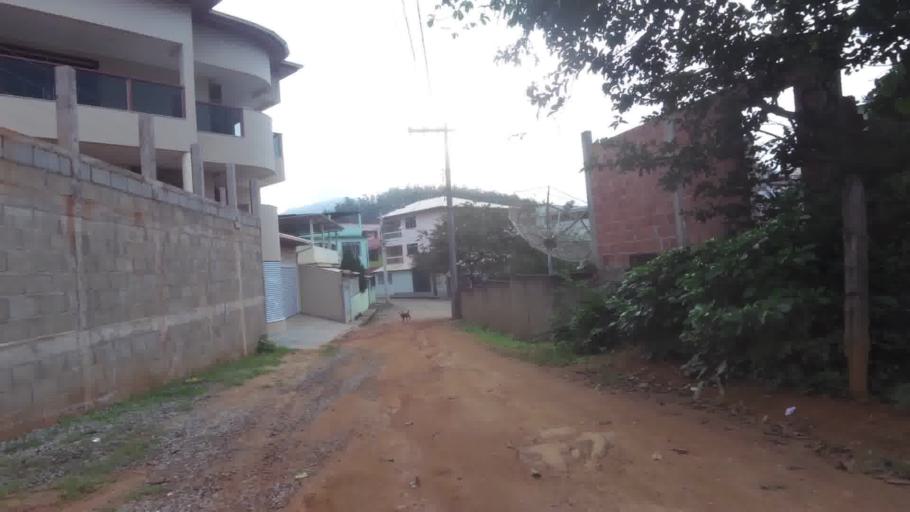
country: BR
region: Espirito Santo
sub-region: Iconha
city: Iconha
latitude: -20.7951
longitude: -40.8091
